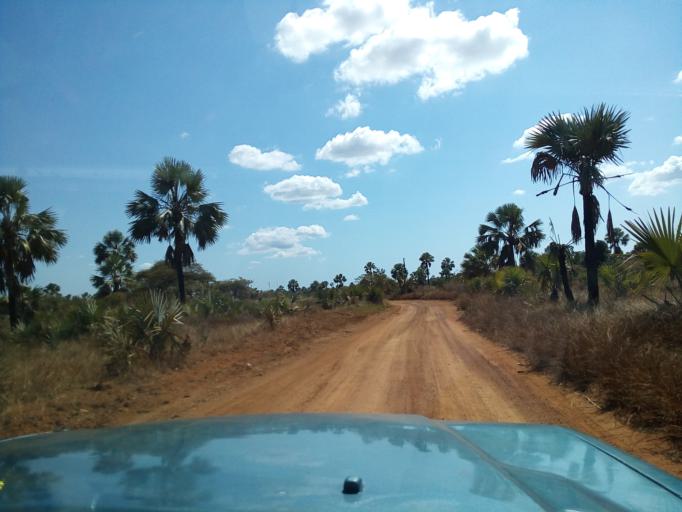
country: MG
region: Boeny
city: Mahajanga
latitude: -15.9719
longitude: 45.9969
